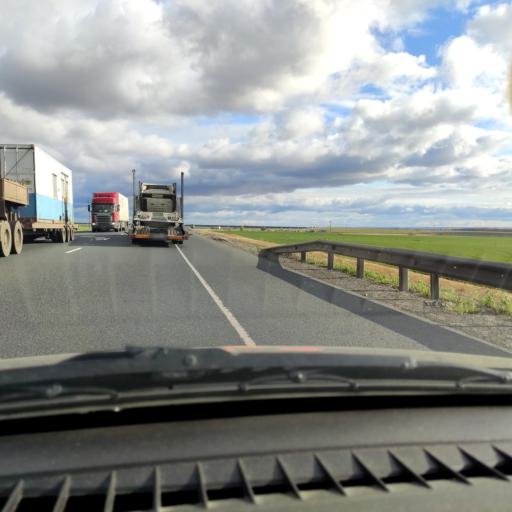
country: RU
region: Samara
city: Varlamovo
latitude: 53.2109
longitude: 48.3973
